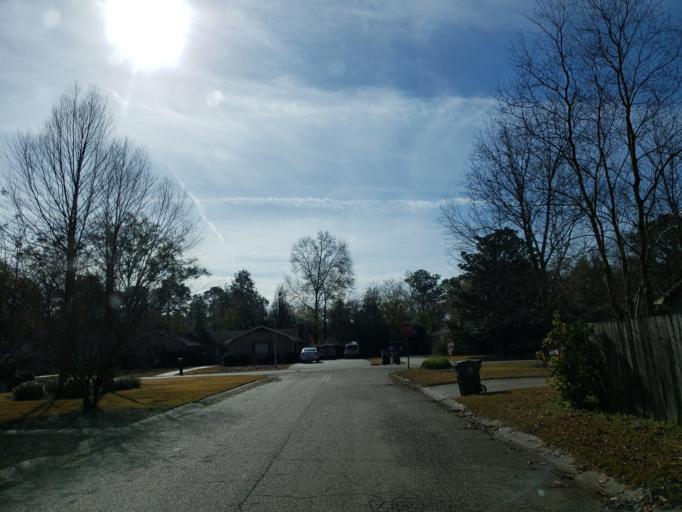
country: US
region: Mississippi
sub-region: Forrest County
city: Hattiesburg
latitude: 31.3068
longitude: -89.3269
